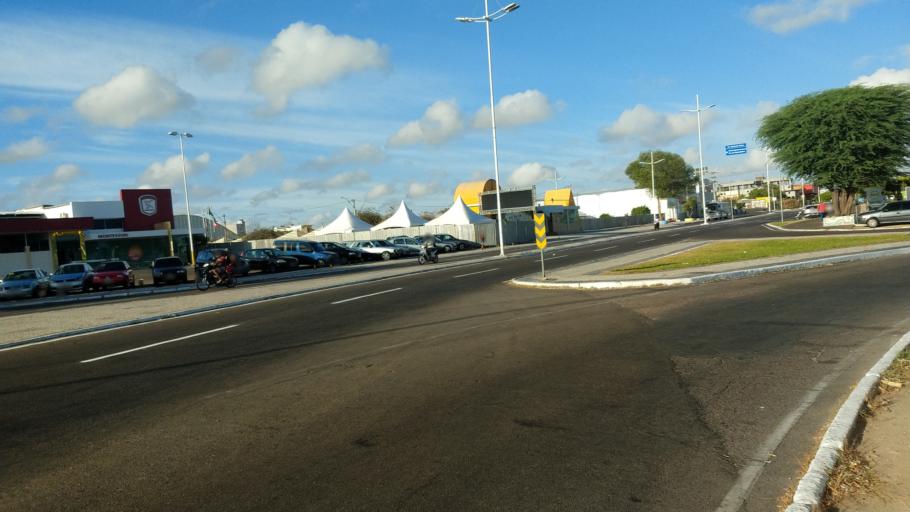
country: BR
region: Bahia
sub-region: Paulo Afonso
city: Paulo Afonso
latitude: -9.3981
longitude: -38.2189
